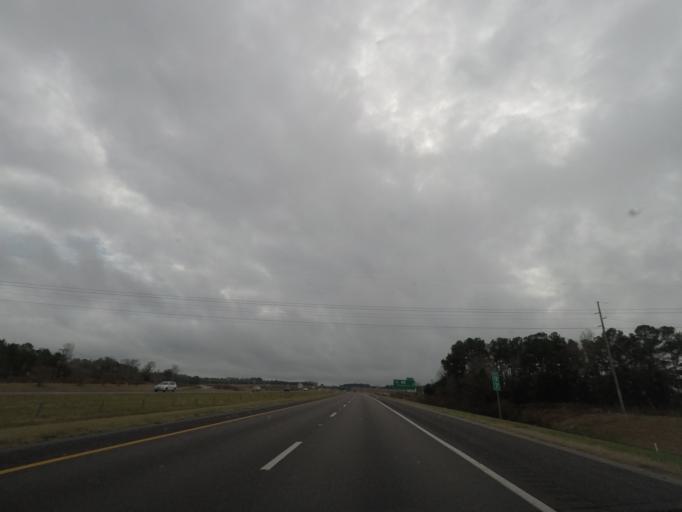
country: US
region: South Carolina
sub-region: Orangeburg County
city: Holly Hill
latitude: 33.4690
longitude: -80.4771
